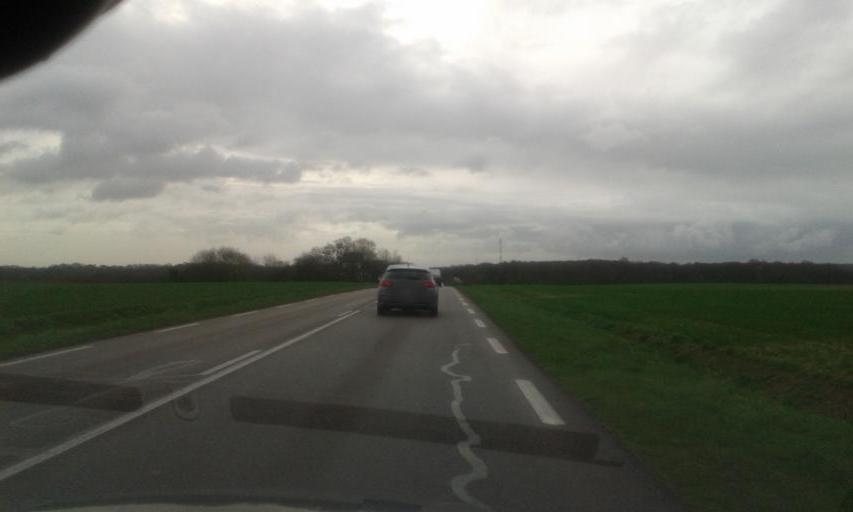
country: FR
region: Haute-Normandie
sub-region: Departement de l'Eure
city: Fleury-sur-Andelle
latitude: 49.3774
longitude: 1.3259
